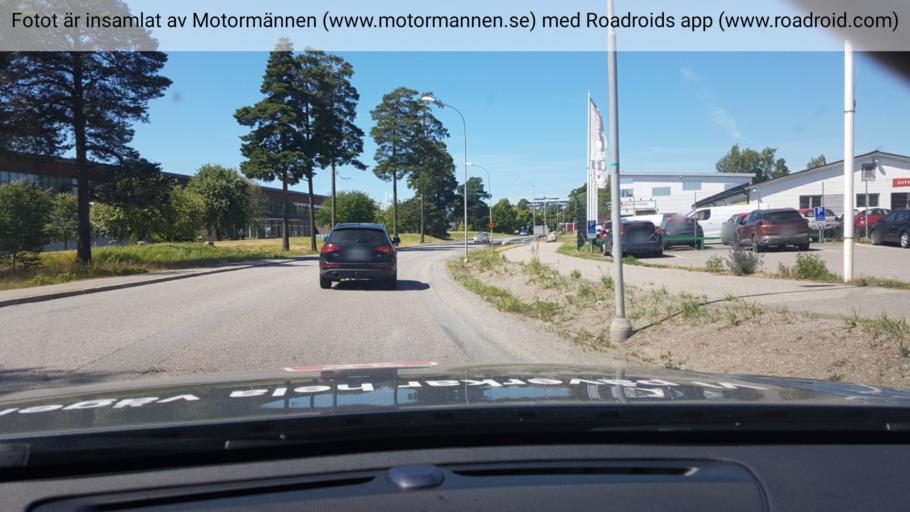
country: SE
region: Stockholm
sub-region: Haninge Kommun
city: Haninge
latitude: 59.1676
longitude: 18.1557
